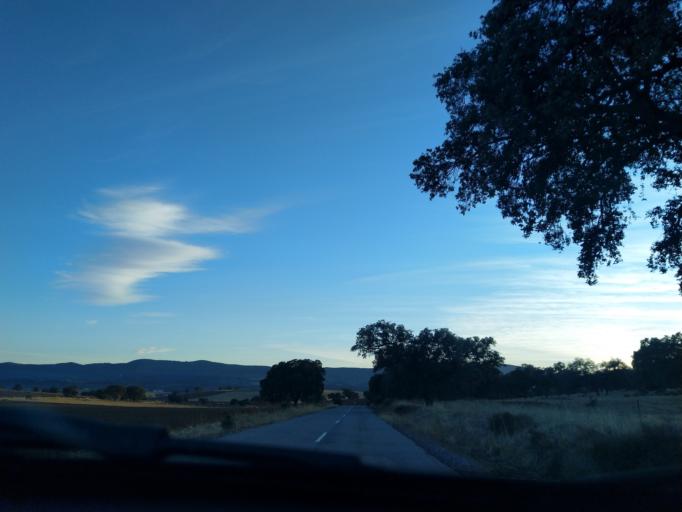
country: ES
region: Extremadura
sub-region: Provincia de Badajoz
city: Valverde de Llerena
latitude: 38.1919
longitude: -5.8549
